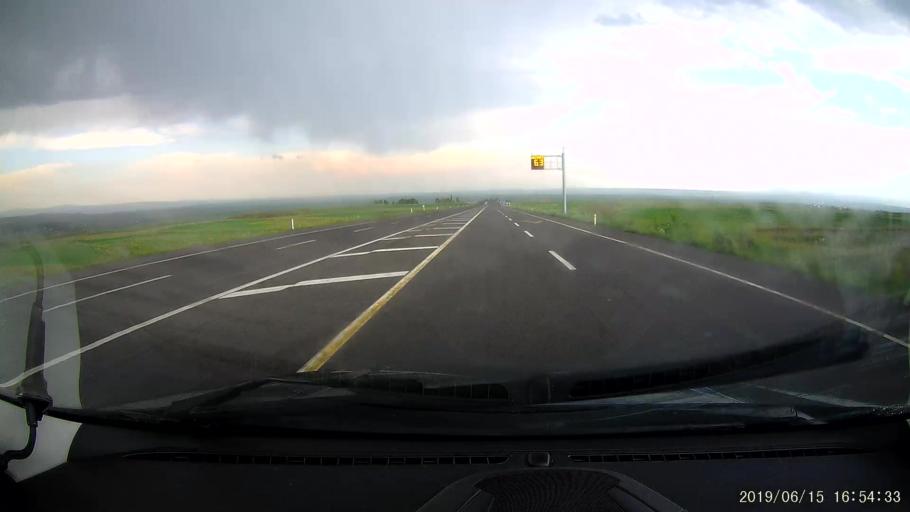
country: TR
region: Kars
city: Susuz
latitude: 40.7898
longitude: 43.1268
